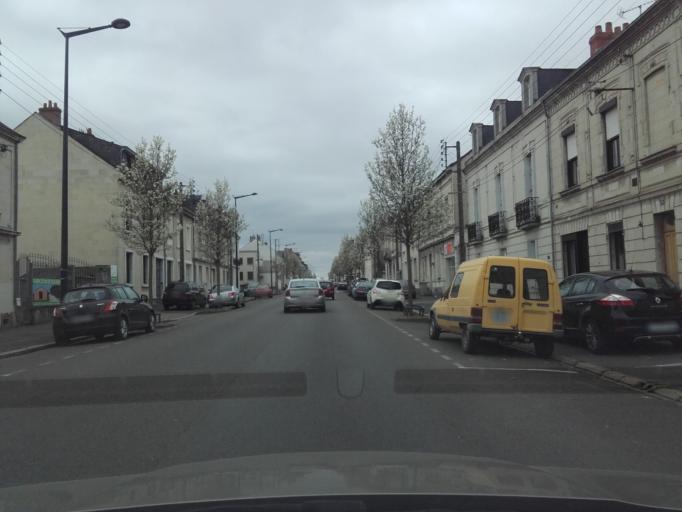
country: FR
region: Pays de la Loire
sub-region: Departement de Maine-et-Loire
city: Saumur
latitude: 47.2713
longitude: -0.0653
